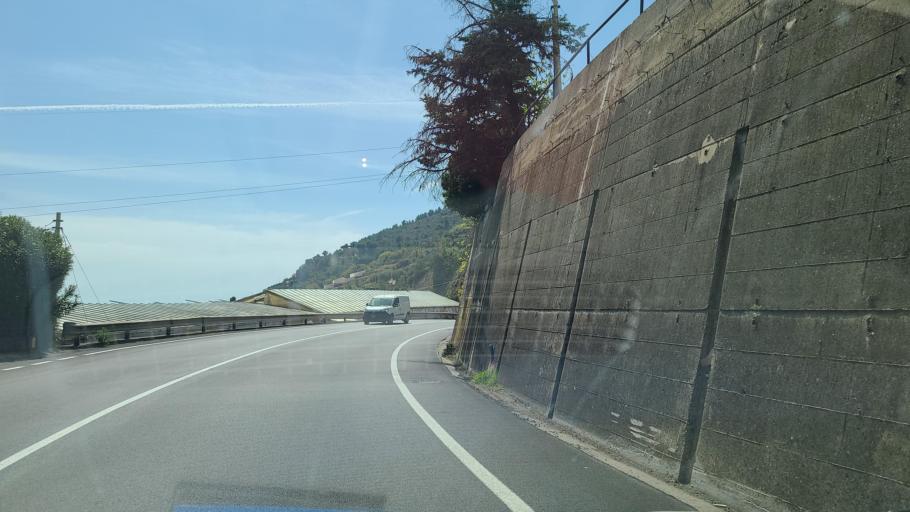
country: IT
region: Liguria
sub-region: Provincia di Imperia
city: Taggia
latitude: 43.8489
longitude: 7.8412
